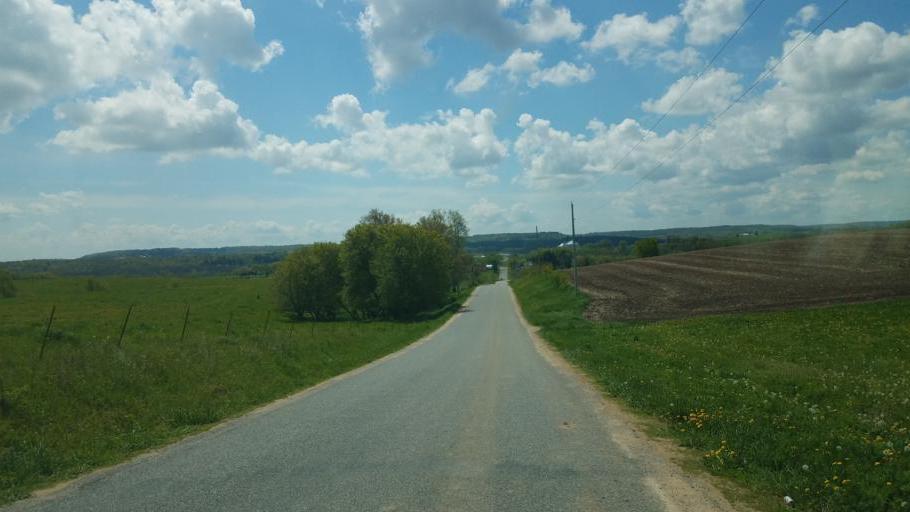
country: US
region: Wisconsin
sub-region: Vernon County
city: Hillsboro
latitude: 43.6847
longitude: -90.3174
